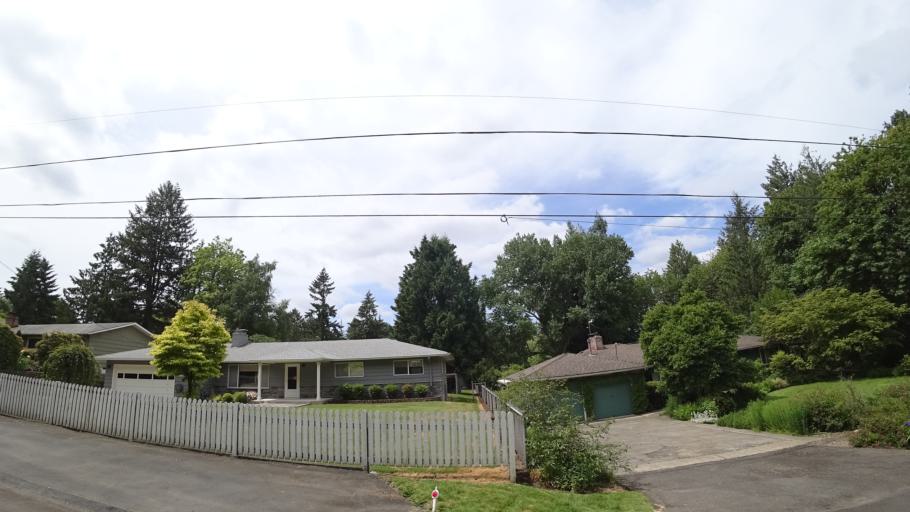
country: US
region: Oregon
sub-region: Washington County
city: Metzger
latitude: 45.4490
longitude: -122.7566
